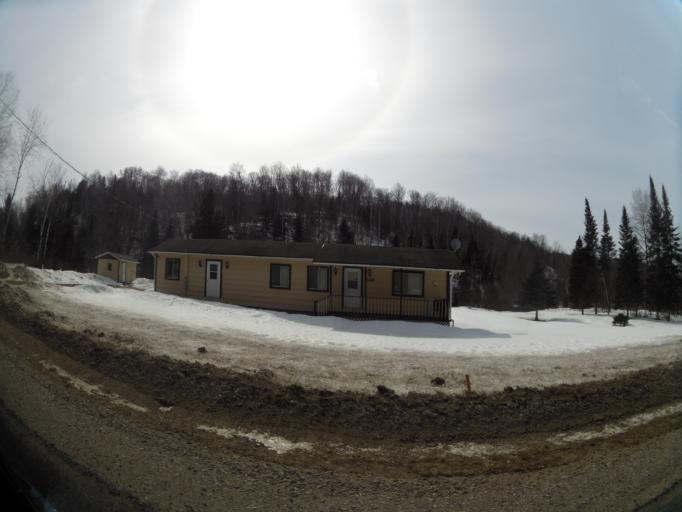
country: CA
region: Quebec
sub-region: Outaouais
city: Val-des-Monts
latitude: 45.9712
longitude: -75.5431
